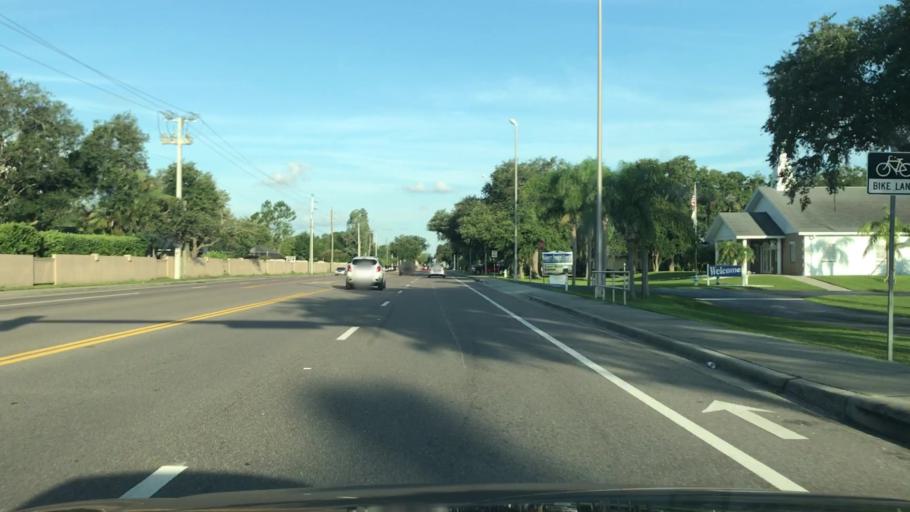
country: US
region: Florida
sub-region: Sarasota County
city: Sarasota Springs
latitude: 27.3231
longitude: -82.4832
